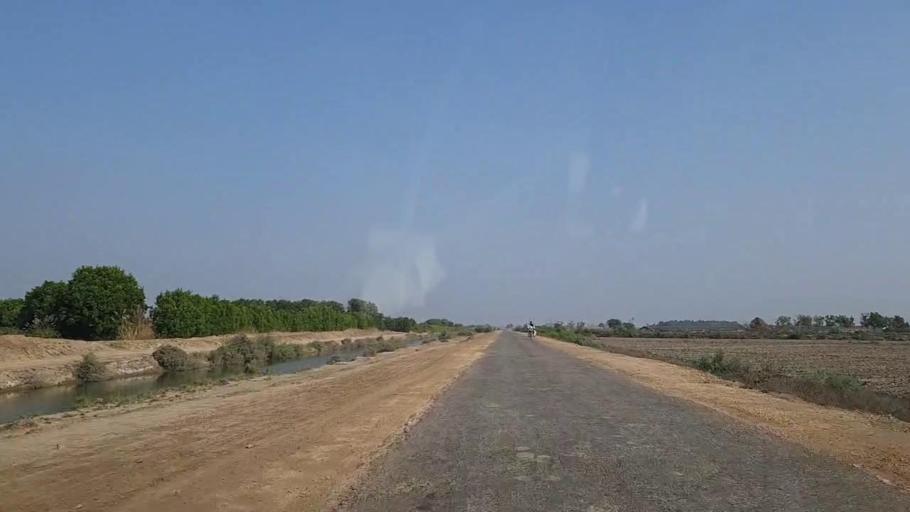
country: PK
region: Sindh
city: Mirpur Sakro
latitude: 24.6363
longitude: 67.6018
